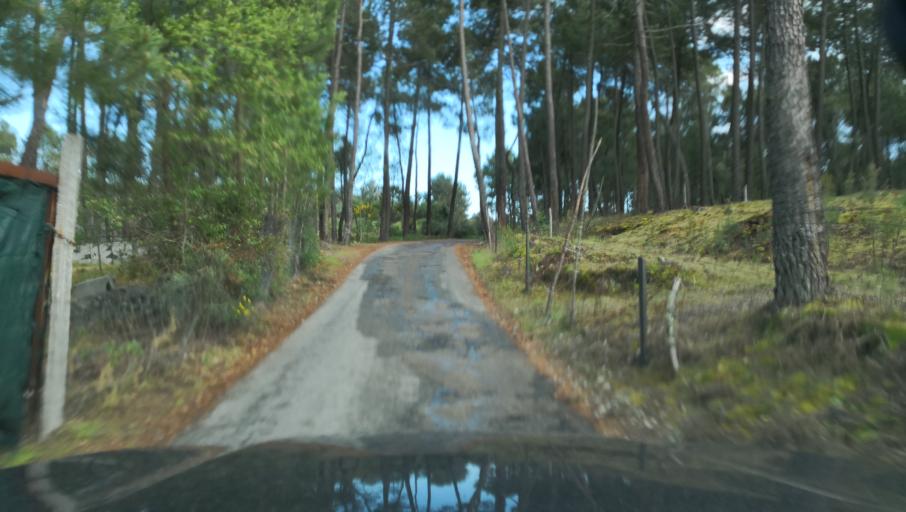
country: PT
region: Vila Real
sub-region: Vila Real
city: Vila Real
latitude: 41.3217
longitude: -7.6906
